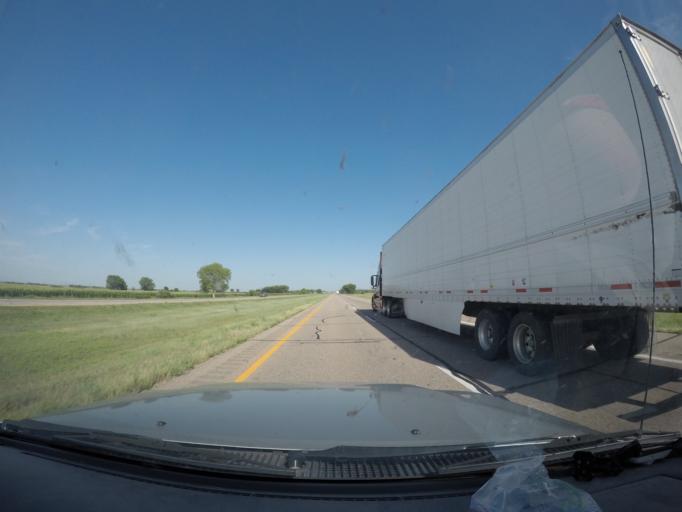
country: US
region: Nebraska
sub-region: Buffalo County
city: Kearney
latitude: 40.6836
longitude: -99.3088
